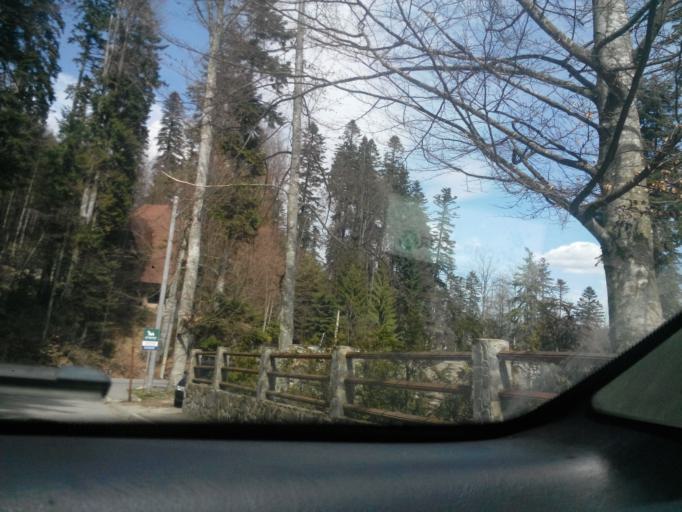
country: RO
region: Prahova
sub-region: Oras Sinaia
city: Sinaia
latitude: 45.3509
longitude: 25.5347
